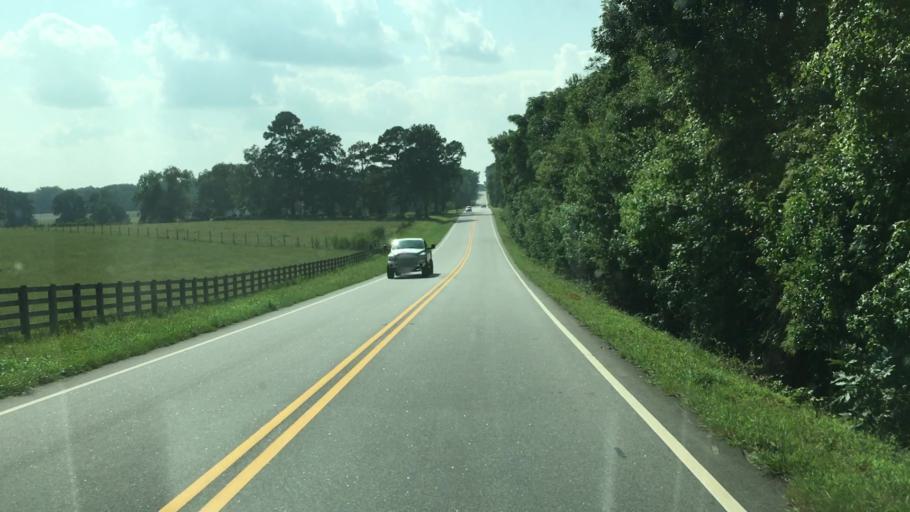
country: US
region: Georgia
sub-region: Jasper County
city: Monticello
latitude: 33.3543
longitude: -83.7322
